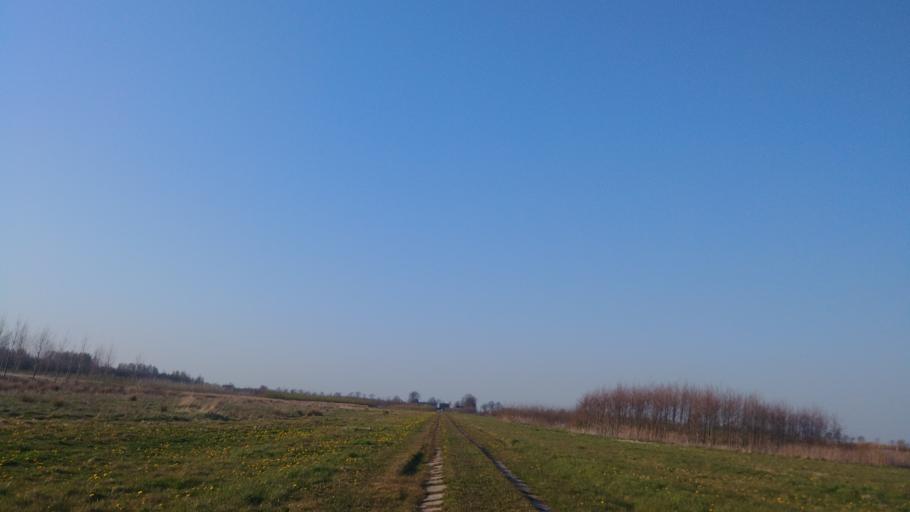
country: NL
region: South Holland
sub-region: Gemeente Waddinxveen
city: Groenswaard
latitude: 52.0691
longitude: 4.6044
